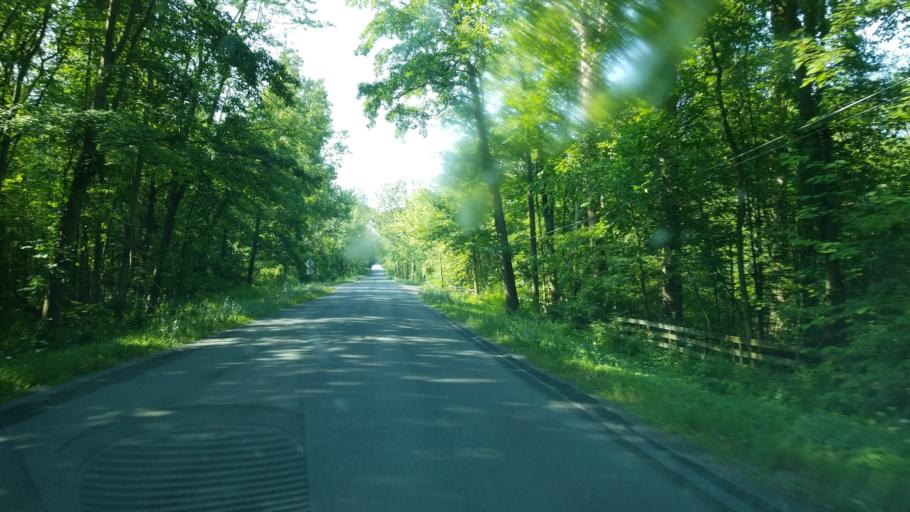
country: US
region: Michigan
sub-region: Kent County
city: Sparta
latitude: 43.1233
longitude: -85.6508
